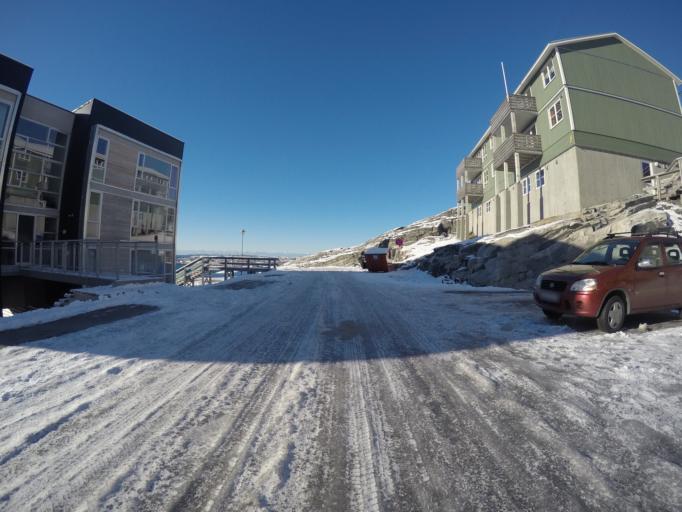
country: GL
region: Sermersooq
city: Nuuk
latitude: 64.1758
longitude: -51.6733
